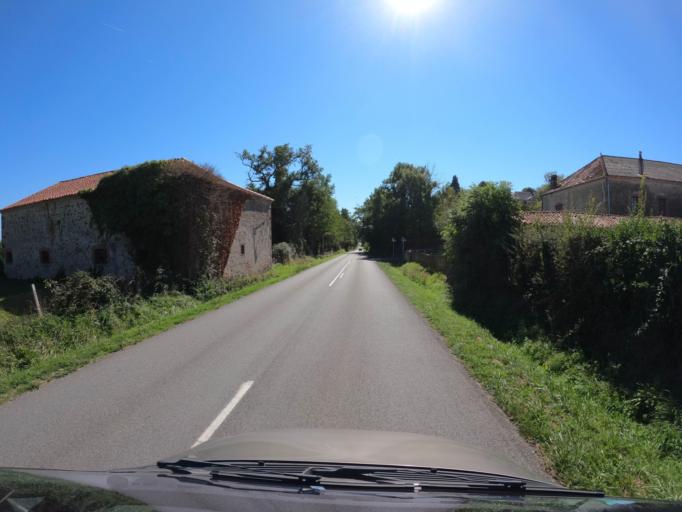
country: FR
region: Limousin
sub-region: Departement de la Haute-Vienne
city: Le Dorat
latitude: 46.2396
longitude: 1.0548
